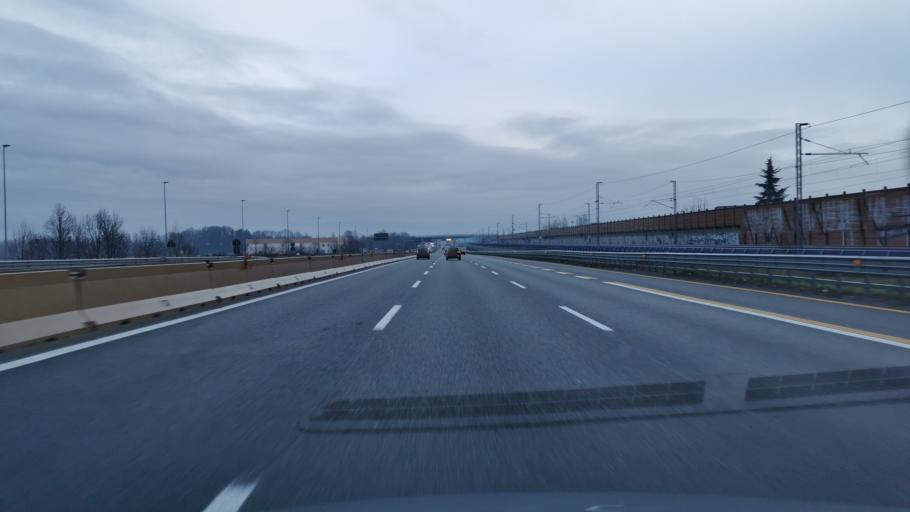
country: IT
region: Piedmont
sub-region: Provincia di Torino
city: Brandizzo
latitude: 45.1826
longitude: 7.8284
